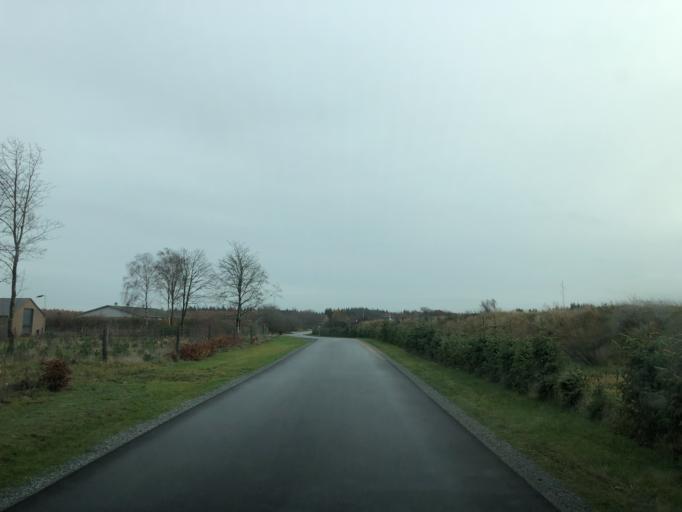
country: DK
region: Central Jutland
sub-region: Ikast-Brande Kommune
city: Bording Kirkeby
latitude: 56.0627
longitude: 9.3711
